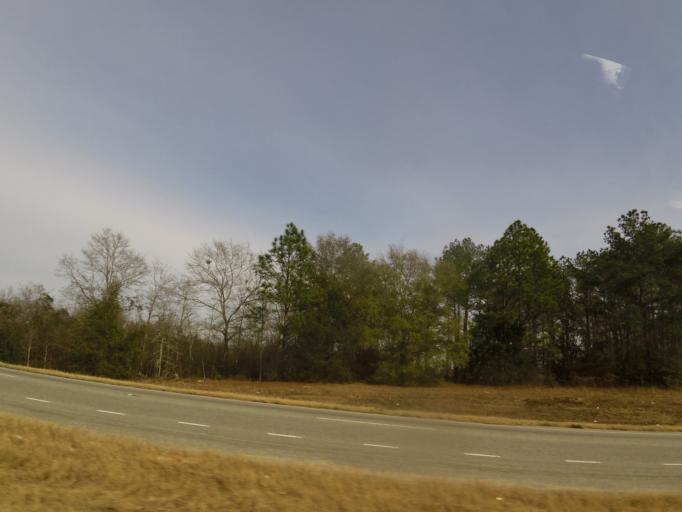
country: US
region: Alabama
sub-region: Dale County
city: Newton
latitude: 31.3905
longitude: -85.5826
